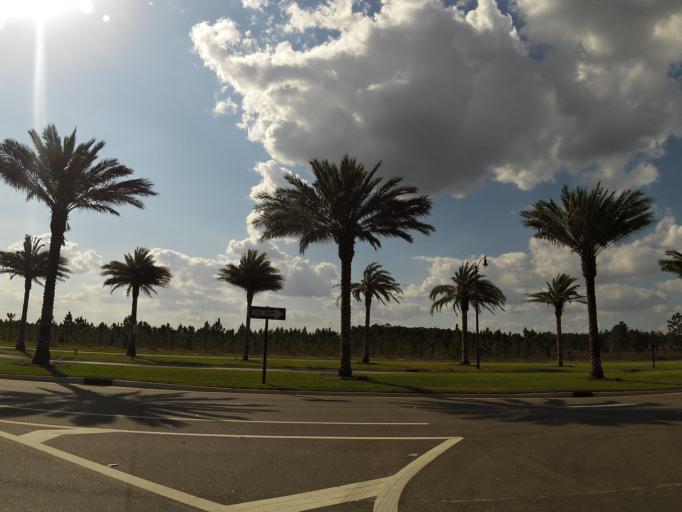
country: US
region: Florida
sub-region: Saint Johns County
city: Palm Valley
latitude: 30.1685
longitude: -81.5063
